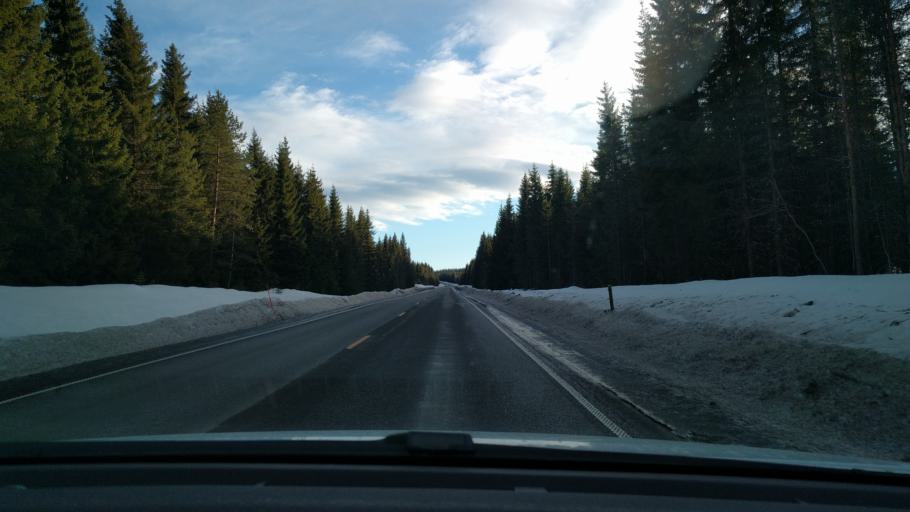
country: NO
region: Hedmark
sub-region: Trysil
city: Innbygda
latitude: 61.0810
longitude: 11.9796
